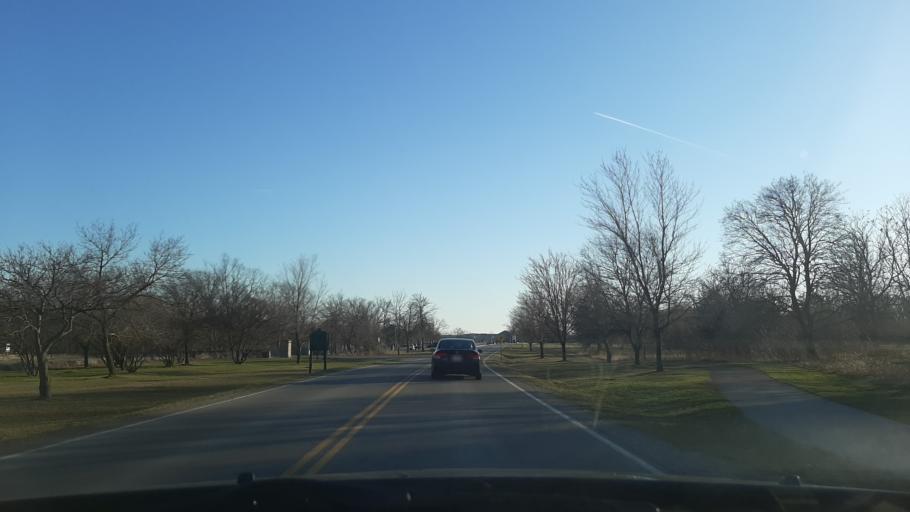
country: CA
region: Ontario
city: Niagara Falls
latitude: 43.1317
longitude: -79.0587
